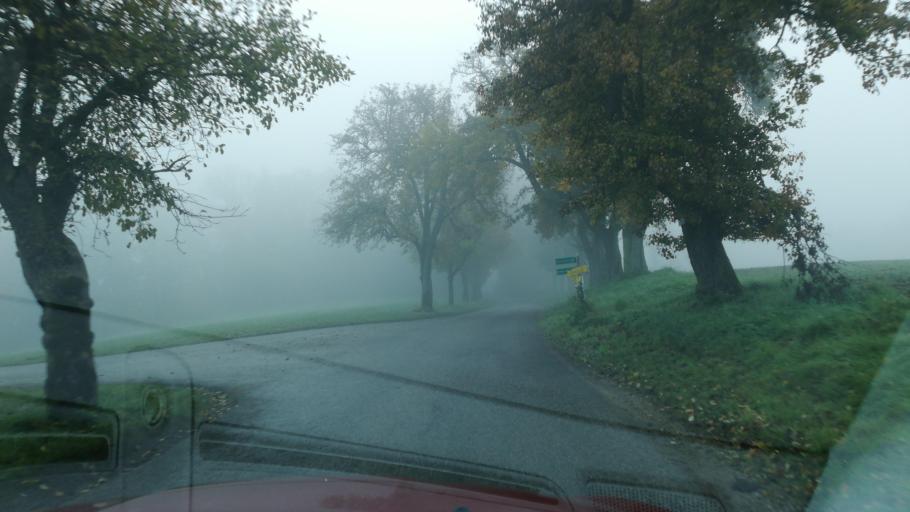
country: AT
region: Upper Austria
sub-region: Politischer Bezirk Grieskirchen
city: Bad Schallerbach
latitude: 48.2074
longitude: 13.8936
